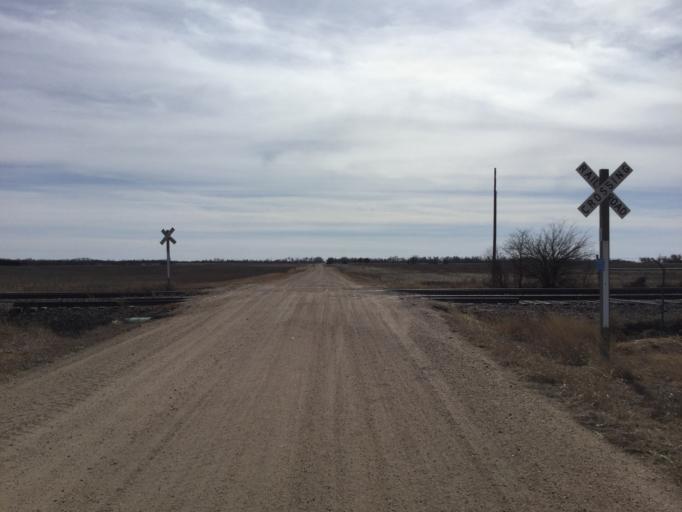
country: US
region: Kansas
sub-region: Barton County
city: Ellinwood
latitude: 38.5148
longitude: -98.3880
